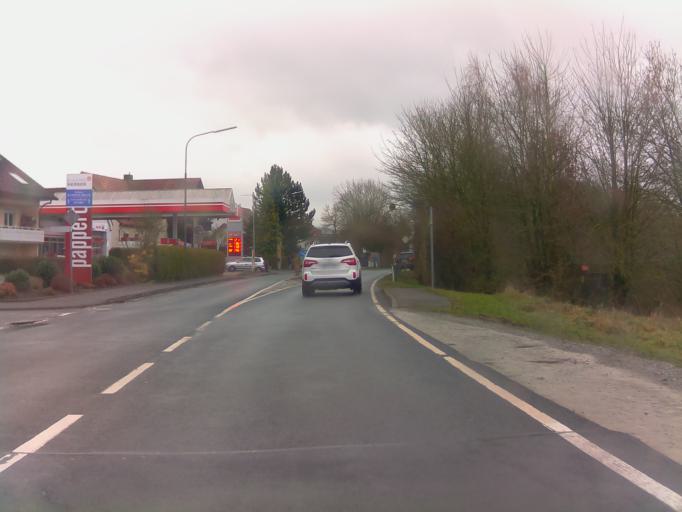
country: DE
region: Hesse
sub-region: Regierungsbezirk Kassel
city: Eichenzell
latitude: 50.4987
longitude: 9.6913
